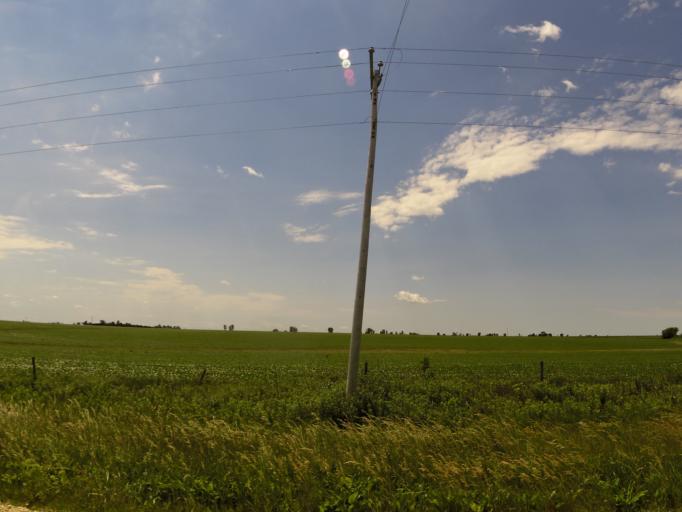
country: US
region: Iowa
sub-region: Bremer County
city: Denver
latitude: 42.7150
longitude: -92.2853
